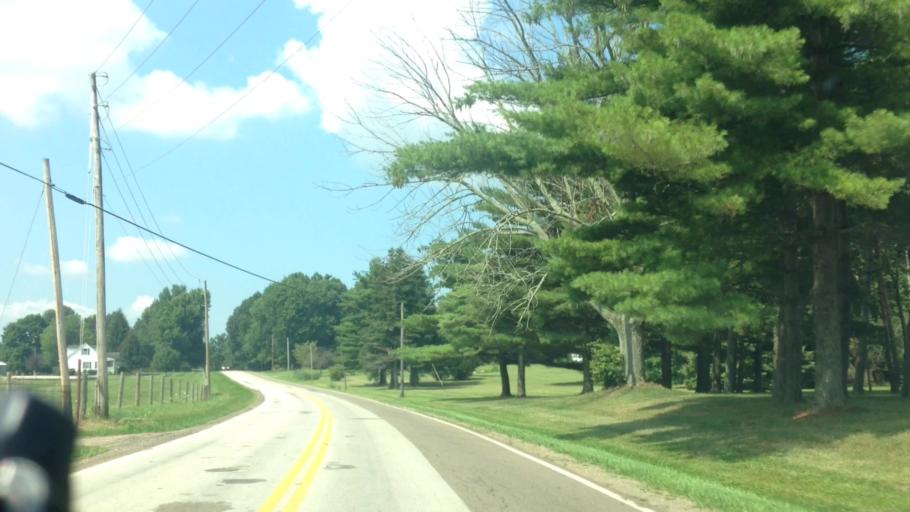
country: US
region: Ohio
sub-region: Wayne County
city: Orrville
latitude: 40.8736
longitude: -81.7502
